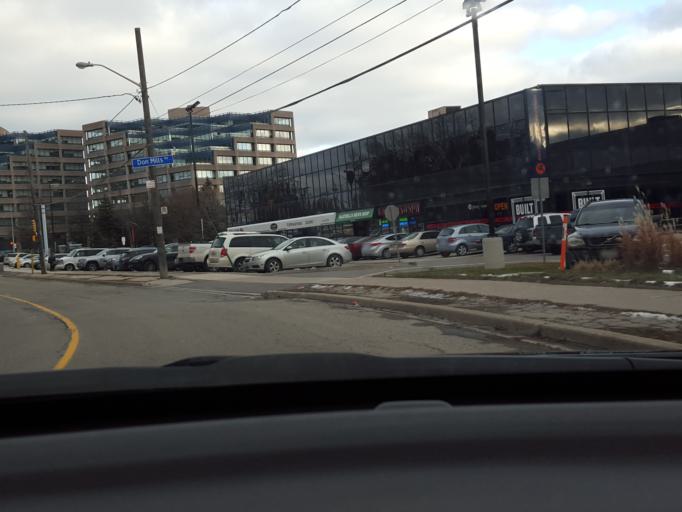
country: CA
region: Ontario
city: Willowdale
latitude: 43.7274
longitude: -79.3423
